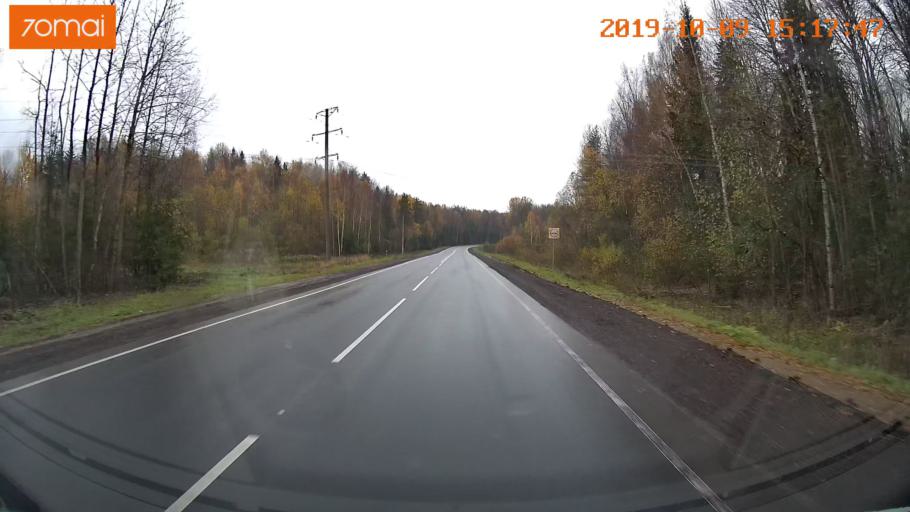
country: RU
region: Kostroma
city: Susanino
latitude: 58.0937
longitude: 41.5815
